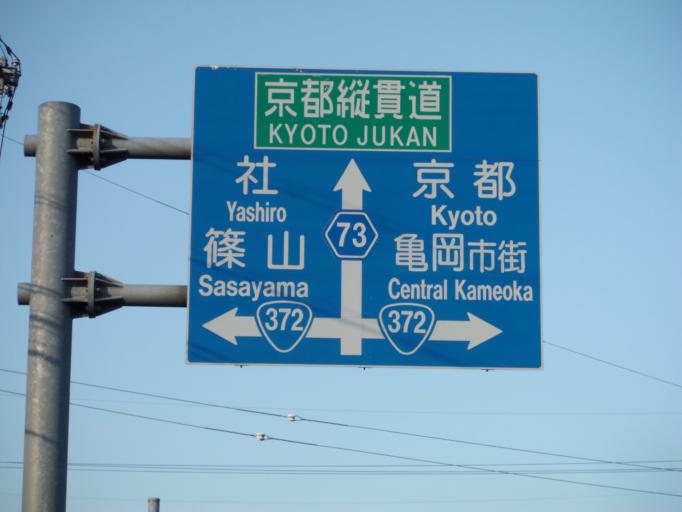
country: JP
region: Kyoto
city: Kameoka
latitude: 35.0425
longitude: 135.4817
